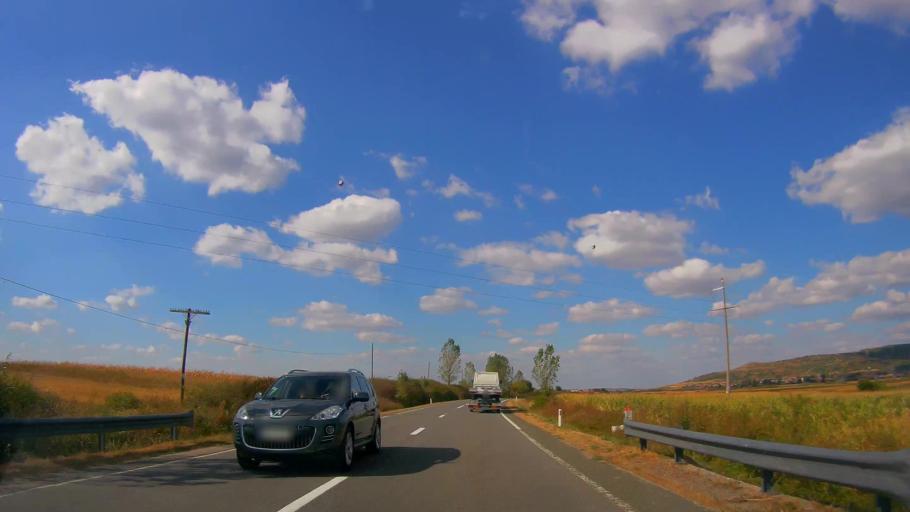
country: RO
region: Salaj
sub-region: Comuna Bobota
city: Dersida
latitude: 47.3693
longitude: 22.7893
